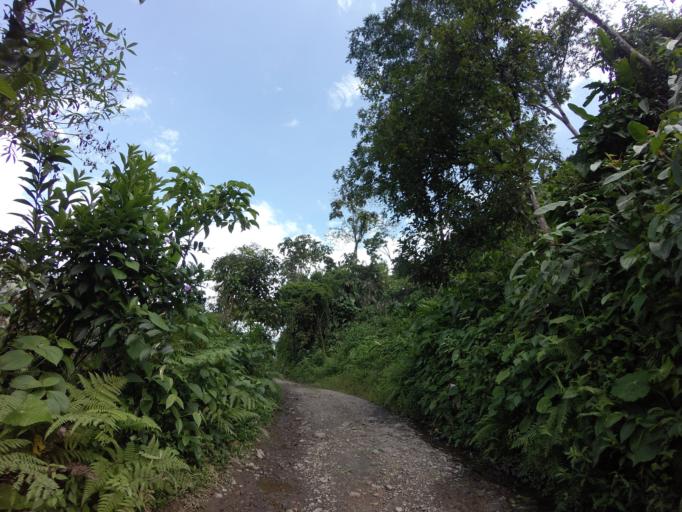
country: CO
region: Antioquia
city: Narino
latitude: 5.5095
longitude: -75.1900
